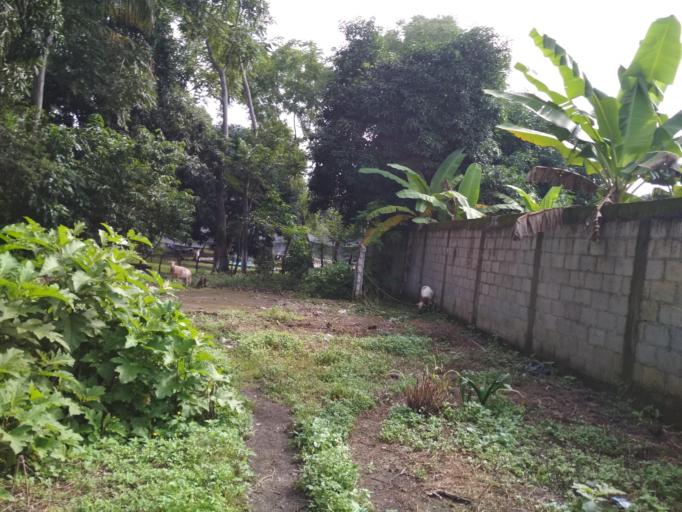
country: MX
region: Veracruz
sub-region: San Andres Tuxtla
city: Matacapan
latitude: 18.4402
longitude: -95.1765
